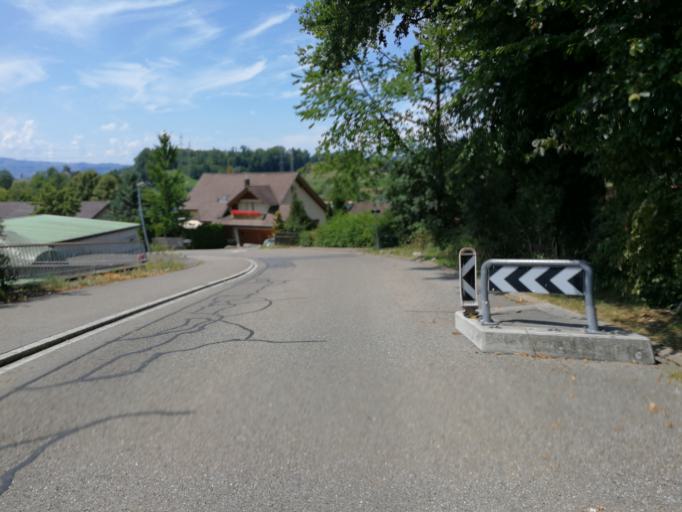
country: CH
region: Zurich
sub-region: Bezirk Hinwil
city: Bubikon
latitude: 47.2646
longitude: 8.8162
